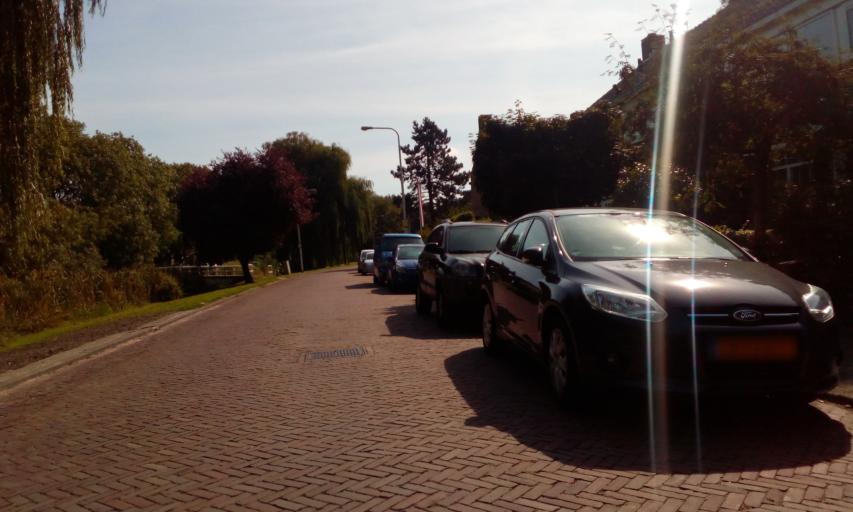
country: NL
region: South Holland
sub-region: Gemeente Voorschoten
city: Voorschoten
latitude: 52.1355
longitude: 4.4521
